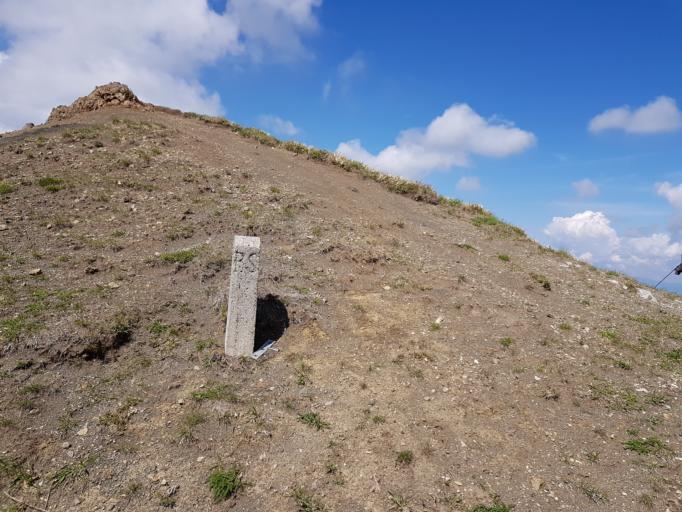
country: IT
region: Liguria
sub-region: Provincia di Genova
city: Santo Stefano d'Aveto
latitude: 44.5554
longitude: 9.4929
